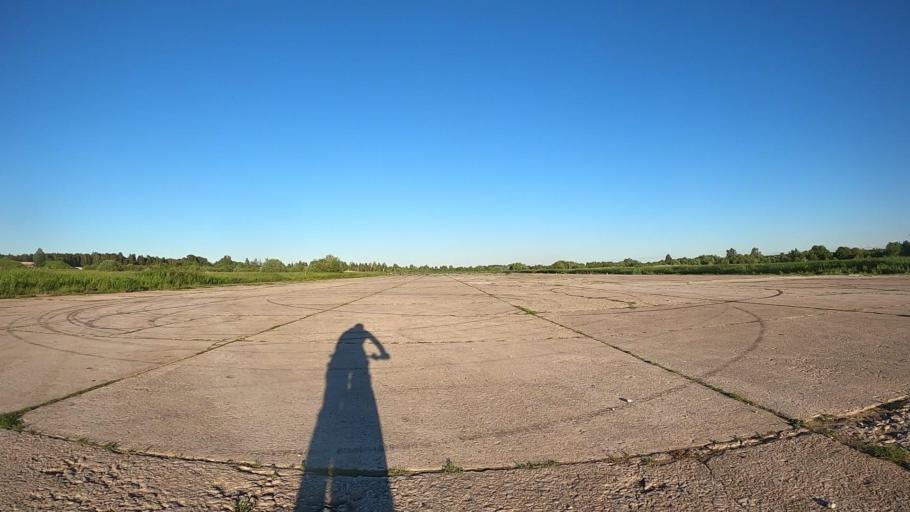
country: LV
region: Kekava
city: Kekava
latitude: 56.8823
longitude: 24.2289
